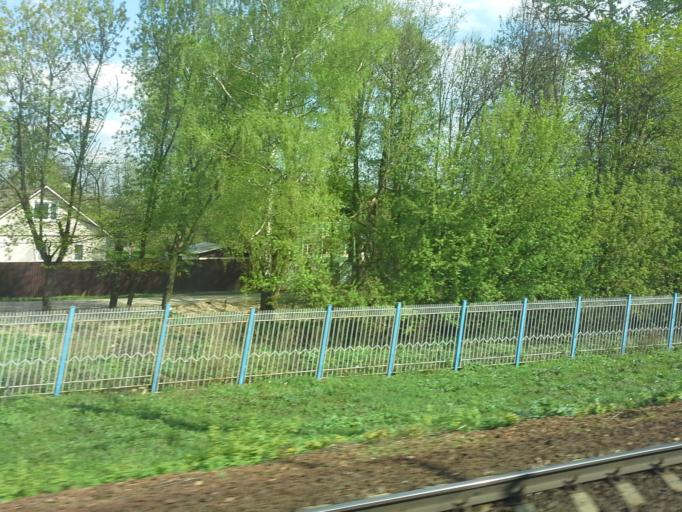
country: RU
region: Moskovskaya
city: Pravdinskiy
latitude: 56.0604
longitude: 37.8654
